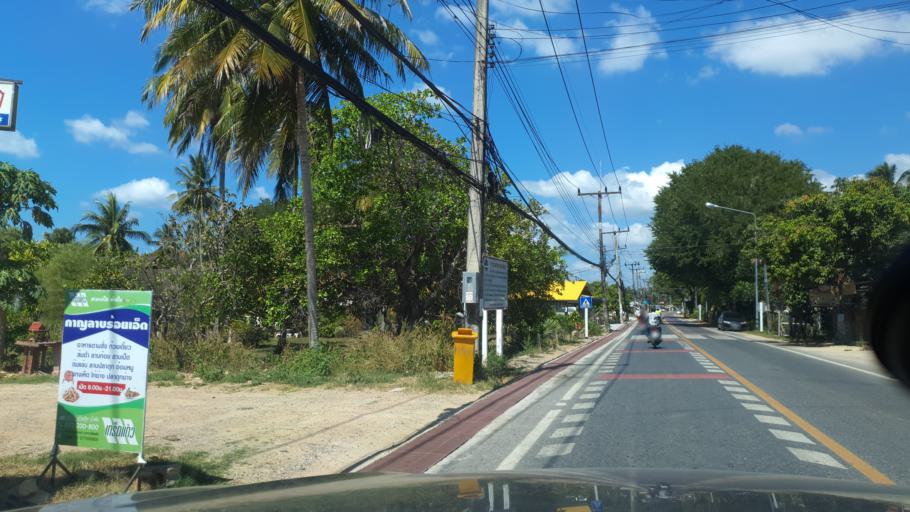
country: TH
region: Phuket
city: Thalang
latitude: 8.1230
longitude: 98.3083
